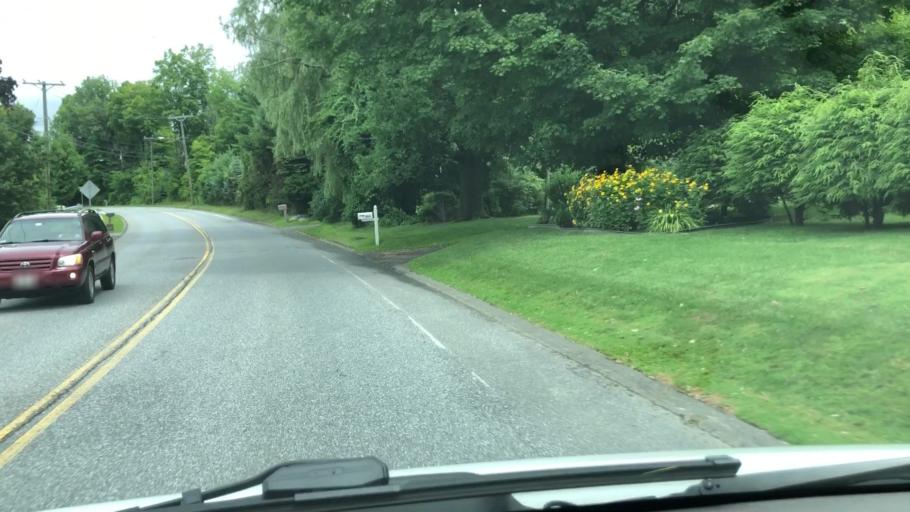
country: US
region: Massachusetts
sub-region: Berkshire County
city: Dalton
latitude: 42.4539
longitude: -73.1840
